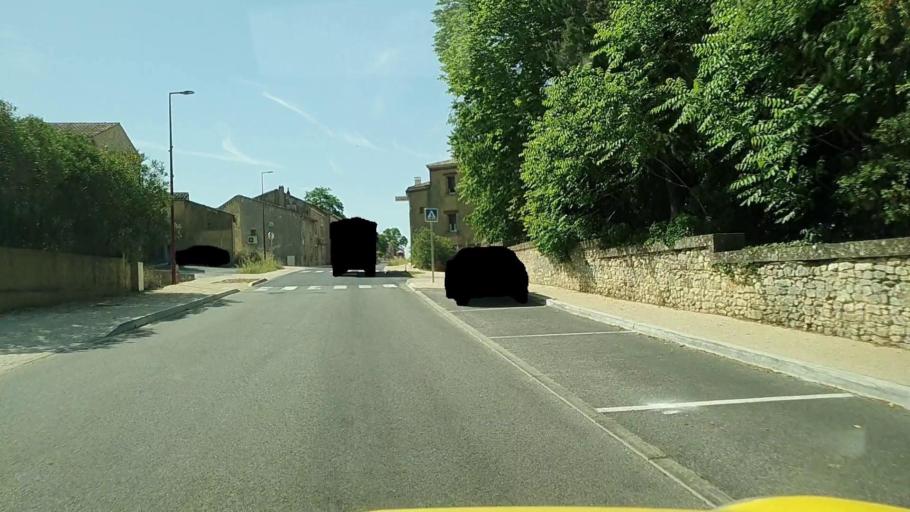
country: FR
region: Languedoc-Roussillon
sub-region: Departement du Gard
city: Connaux
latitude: 44.0424
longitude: 4.5801
